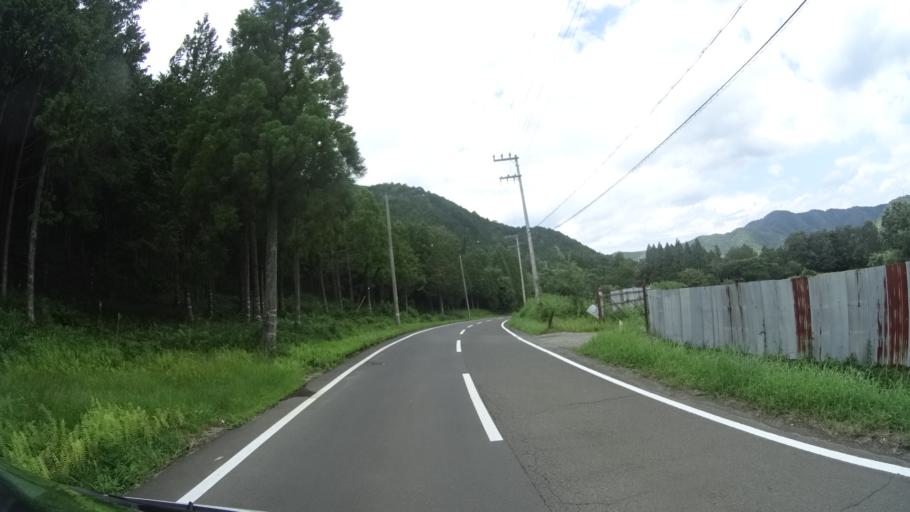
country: JP
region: Kyoto
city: Ayabe
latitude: 35.2882
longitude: 135.3293
